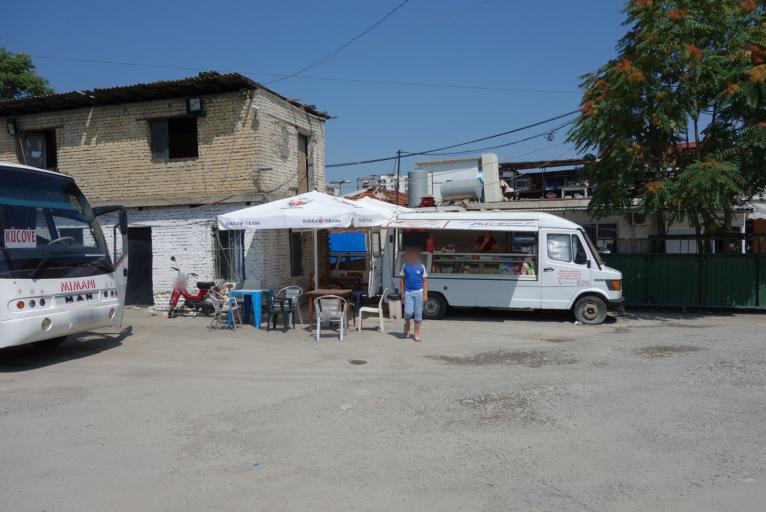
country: AL
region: Tirane
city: Tirana
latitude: 41.3214
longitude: 19.7984
